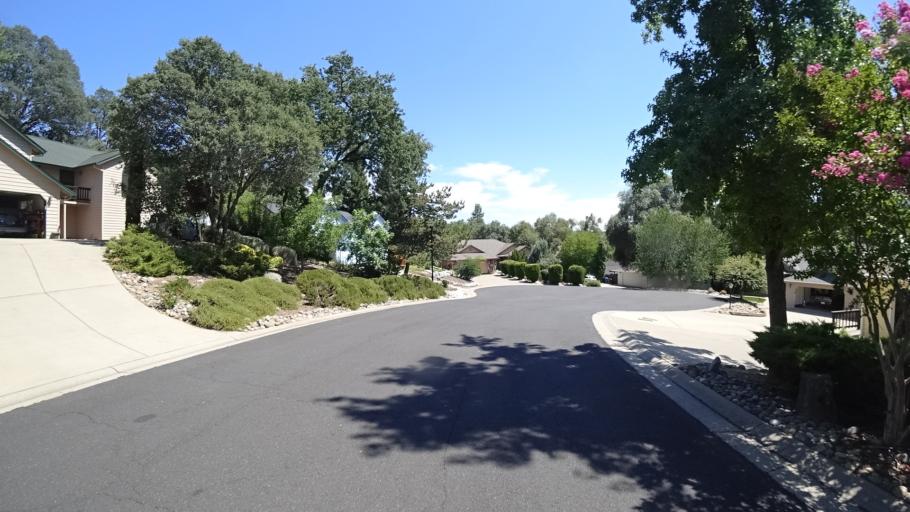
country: US
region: California
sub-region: Calaveras County
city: Angels Camp
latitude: 38.0757
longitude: -120.5596
